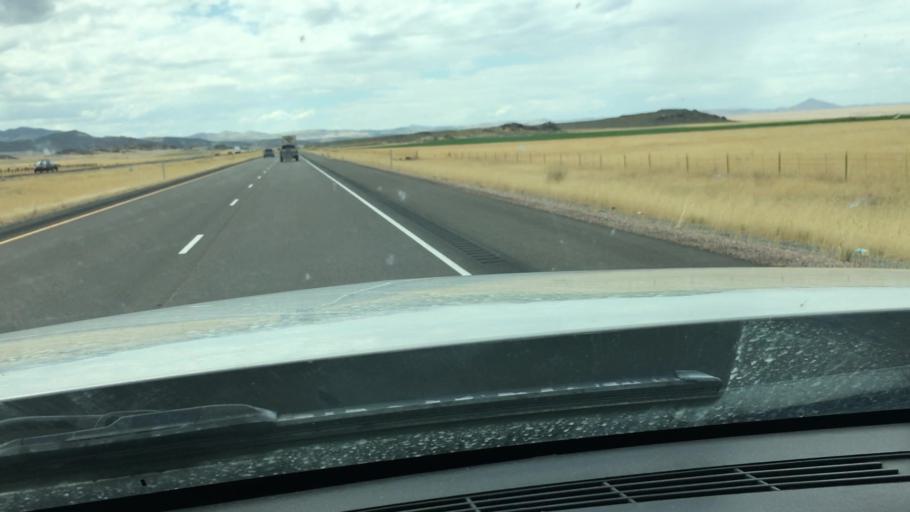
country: US
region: Utah
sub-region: Millard County
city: Fillmore
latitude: 38.8322
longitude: -112.4813
